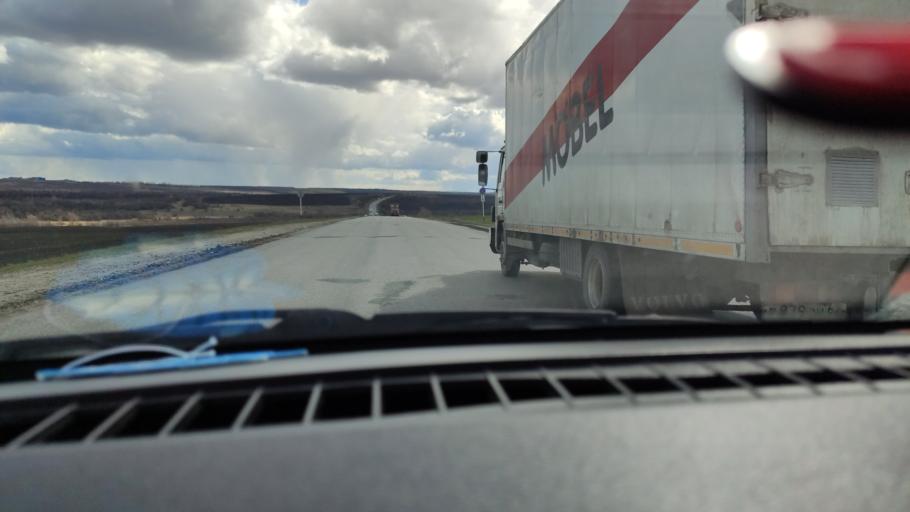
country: RU
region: Samara
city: Varlamovo
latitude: 53.0769
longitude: 48.3541
